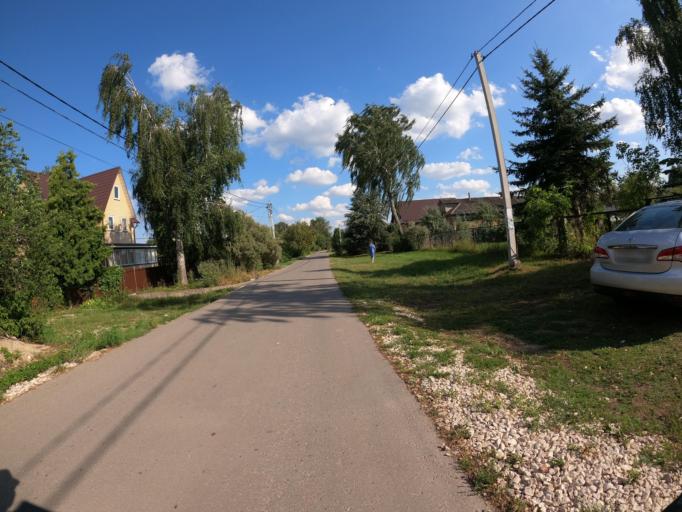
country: RU
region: Moskovskaya
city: Peski
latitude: 55.2109
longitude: 38.7370
